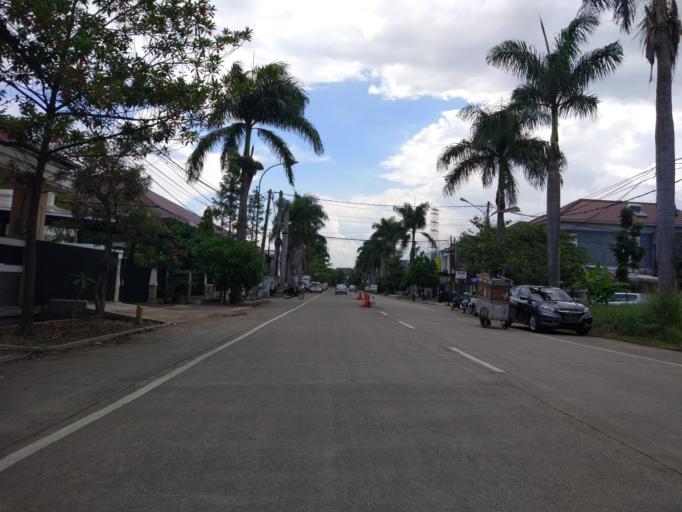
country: ID
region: West Java
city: Bandung
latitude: -6.9213
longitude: 107.6711
